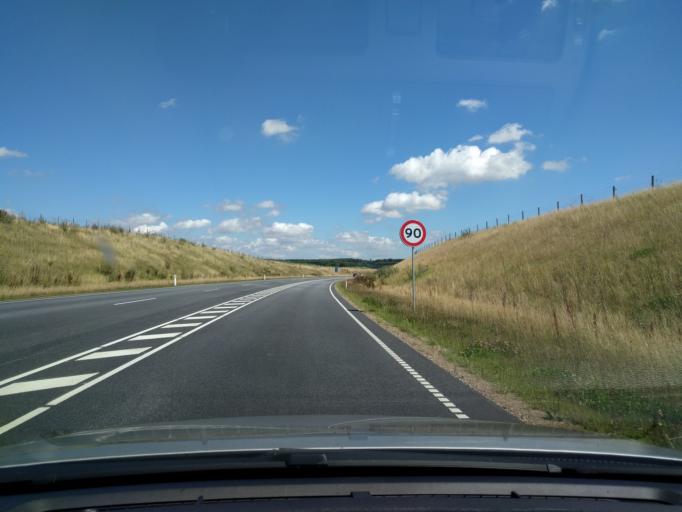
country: DK
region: Zealand
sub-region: Naestved Kommune
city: Naestved
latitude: 55.2605
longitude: 11.7382
